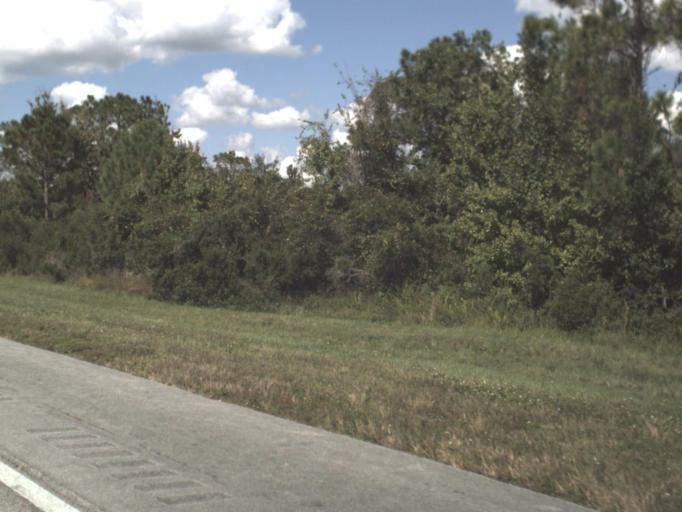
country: US
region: Florida
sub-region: Indian River County
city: Fellsmere
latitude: 27.6660
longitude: -80.8745
